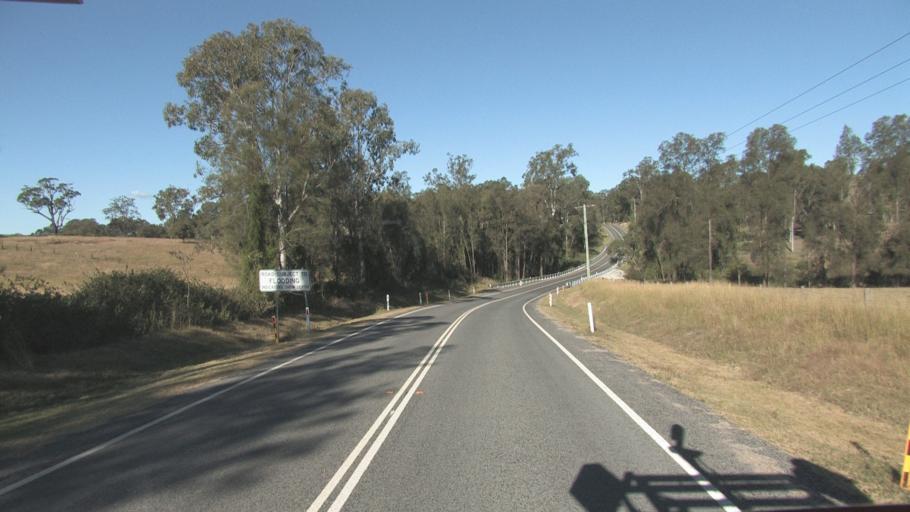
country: AU
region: Queensland
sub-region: Logan
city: Chambers Flat
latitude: -27.7721
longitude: 153.0710
